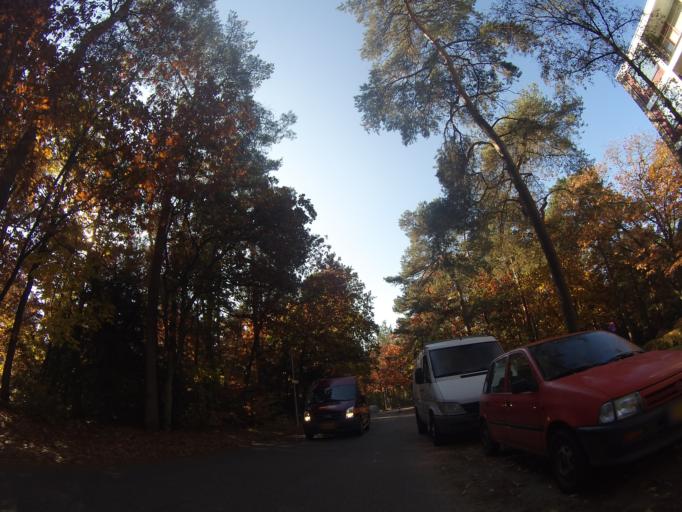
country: NL
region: Utrecht
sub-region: Gemeente Utrechtse Heuvelrug
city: Driebergen-Rijsenburg
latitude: 52.0723
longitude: 5.2637
